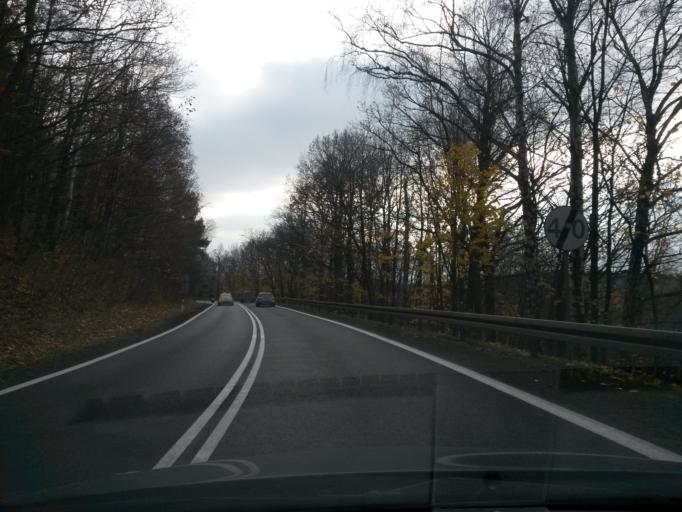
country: PL
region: Lower Silesian Voivodeship
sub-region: Powiat jaworski
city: Bolkow
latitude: 50.9343
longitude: 16.0714
